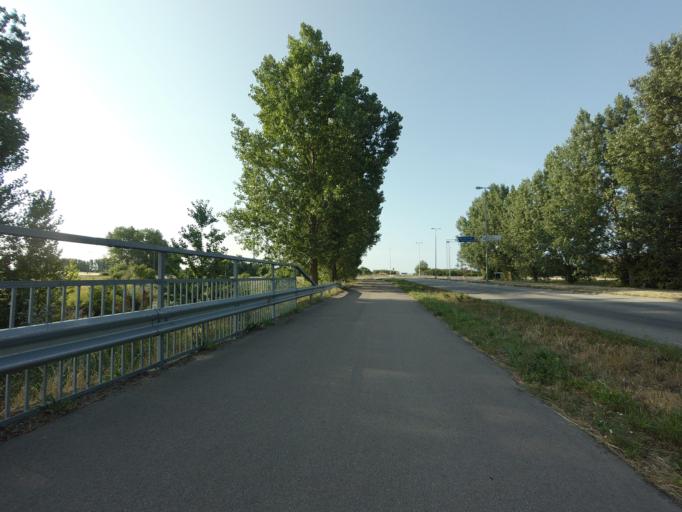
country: SE
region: Skane
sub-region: Landskrona
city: Landskrona
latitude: 55.8657
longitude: 12.8703
